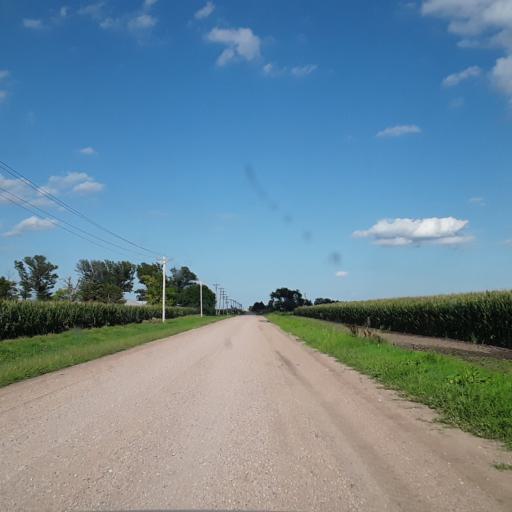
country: US
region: Nebraska
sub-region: Hall County
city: Wood River
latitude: 40.9167
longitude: -98.5664
